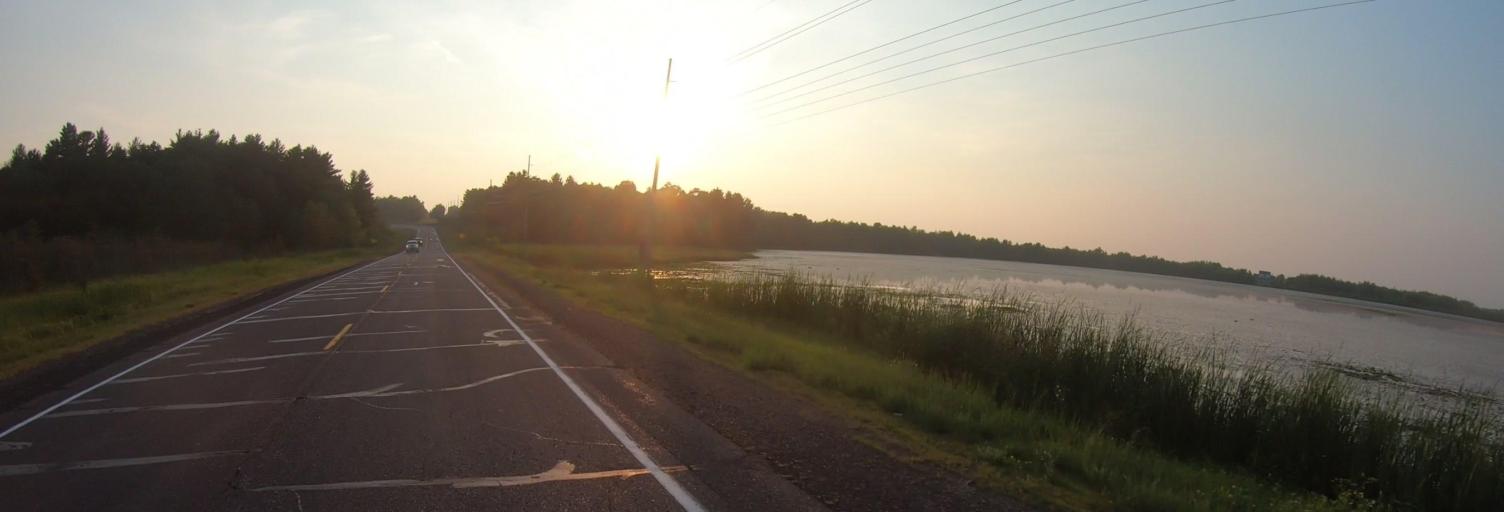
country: US
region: Wisconsin
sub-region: Burnett County
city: Siren
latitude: 45.7843
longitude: -92.4147
